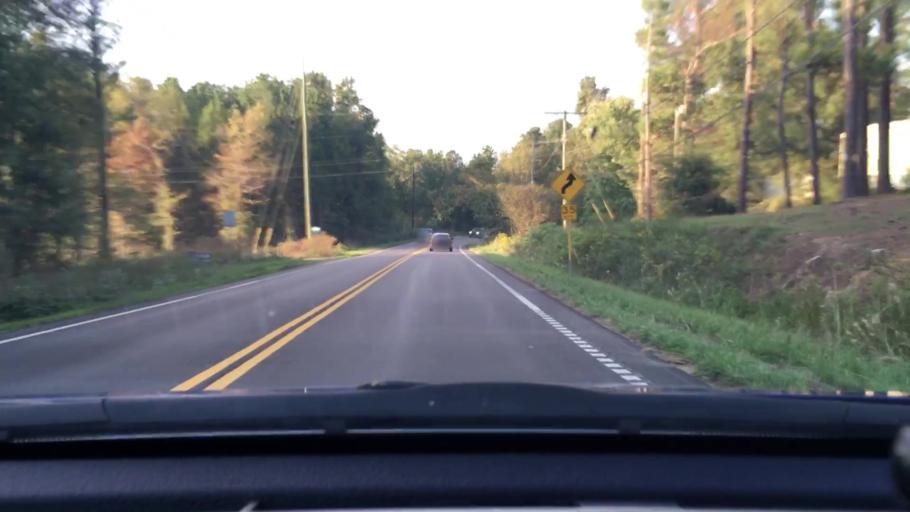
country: US
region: South Carolina
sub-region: Lexington County
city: Irmo
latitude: 34.1068
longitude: -81.1614
